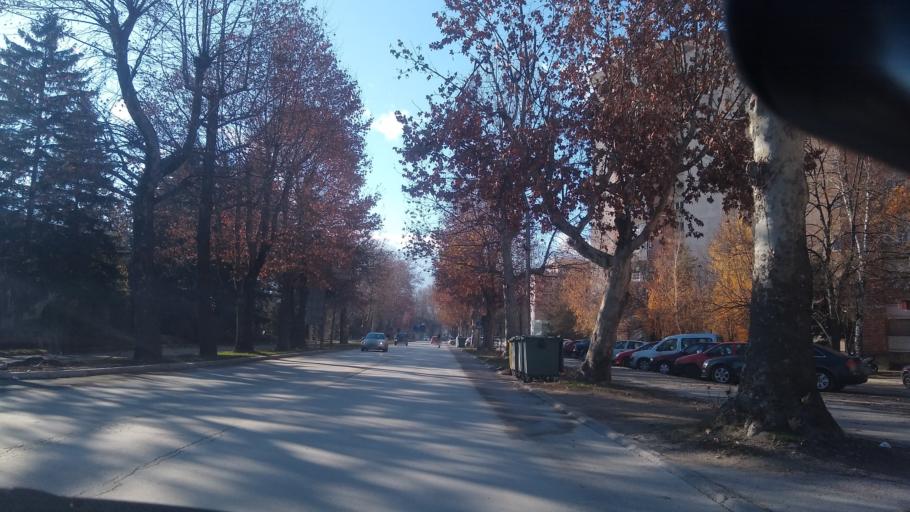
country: MK
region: Bitola
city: Bitola
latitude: 41.0232
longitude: 21.3358
